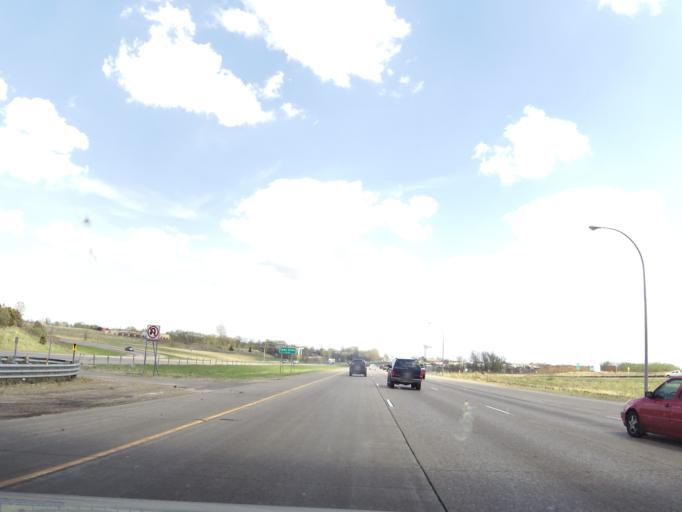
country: US
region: Minnesota
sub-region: Washington County
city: Oakdale
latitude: 44.9485
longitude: -92.9344
